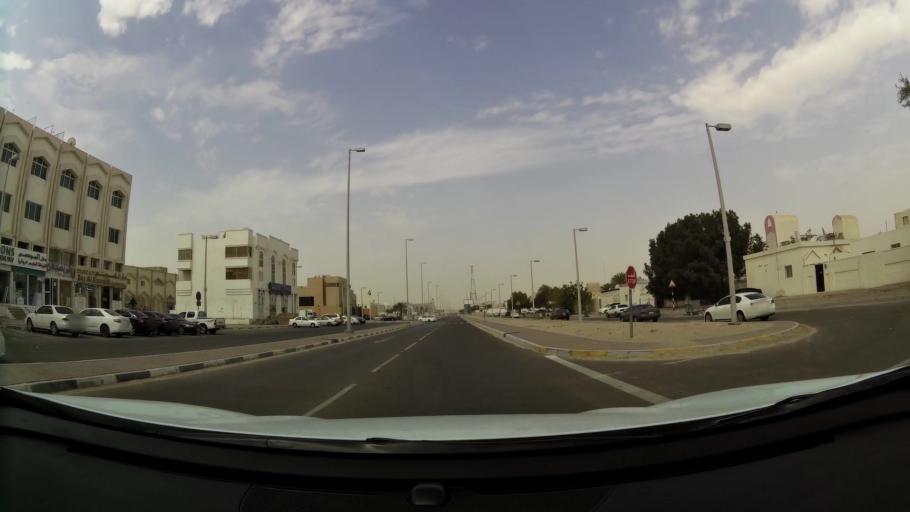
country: AE
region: Abu Dhabi
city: Abu Dhabi
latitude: 24.3067
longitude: 54.6123
